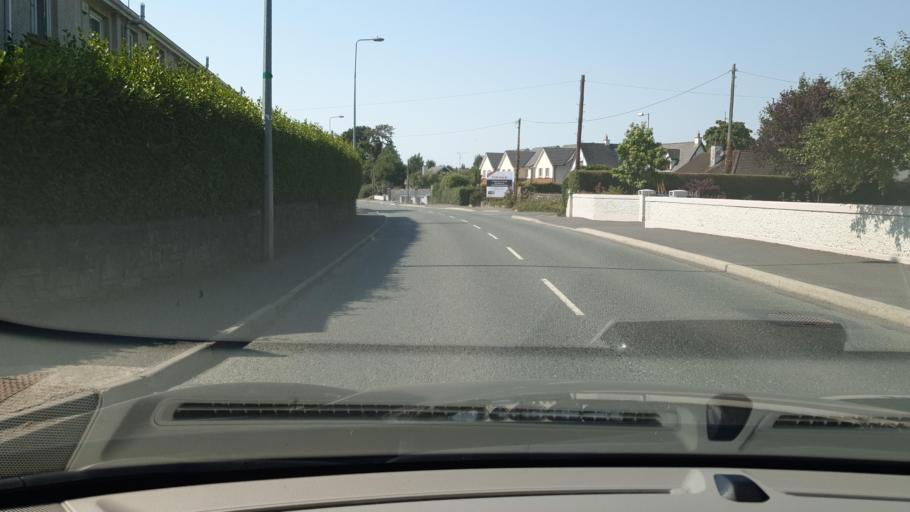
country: IE
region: Leinster
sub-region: An Mhi
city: Ratoath
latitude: 53.5078
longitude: -6.4664
